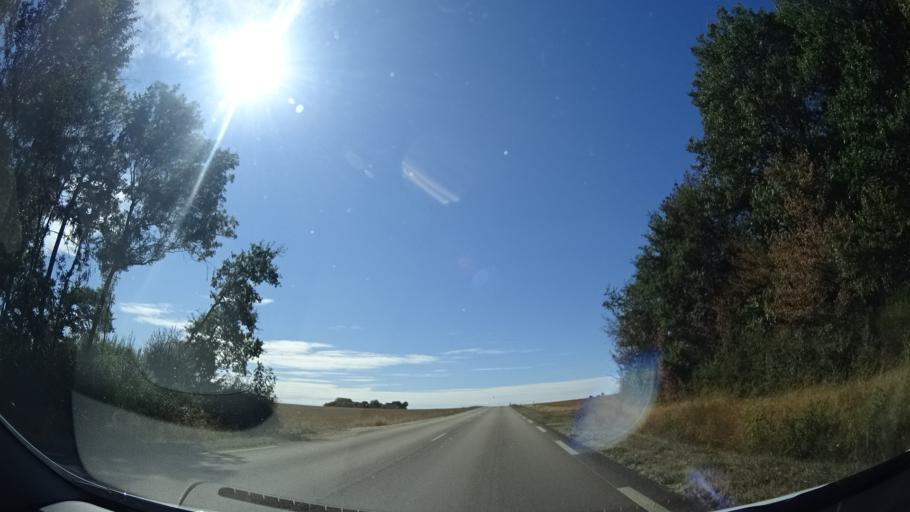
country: FR
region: Bourgogne
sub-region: Departement de l'Yonne
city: Charny
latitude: 47.9298
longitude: 3.1914
